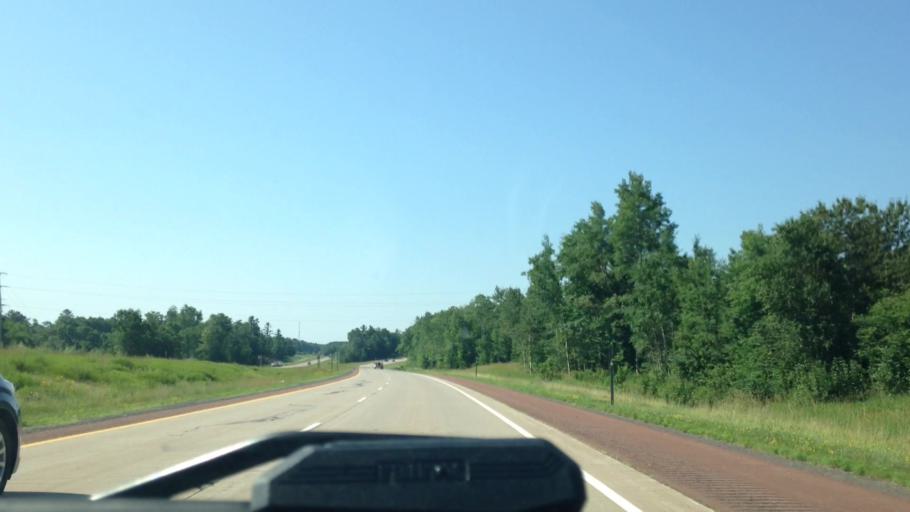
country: US
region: Wisconsin
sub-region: Douglas County
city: Lake Nebagamon
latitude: 46.3958
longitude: -91.8189
